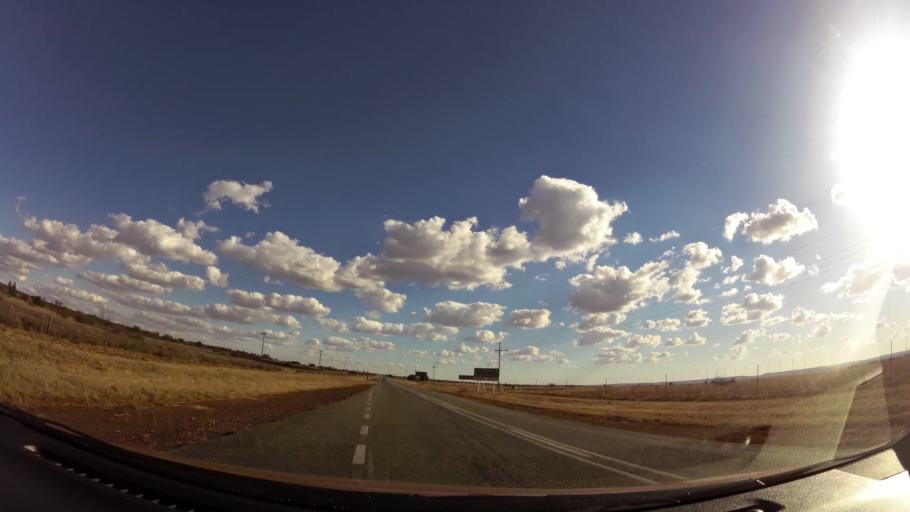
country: ZA
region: Gauteng
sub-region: West Rand District Municipality
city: Carletonville
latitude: -26.4138
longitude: 27.2344
